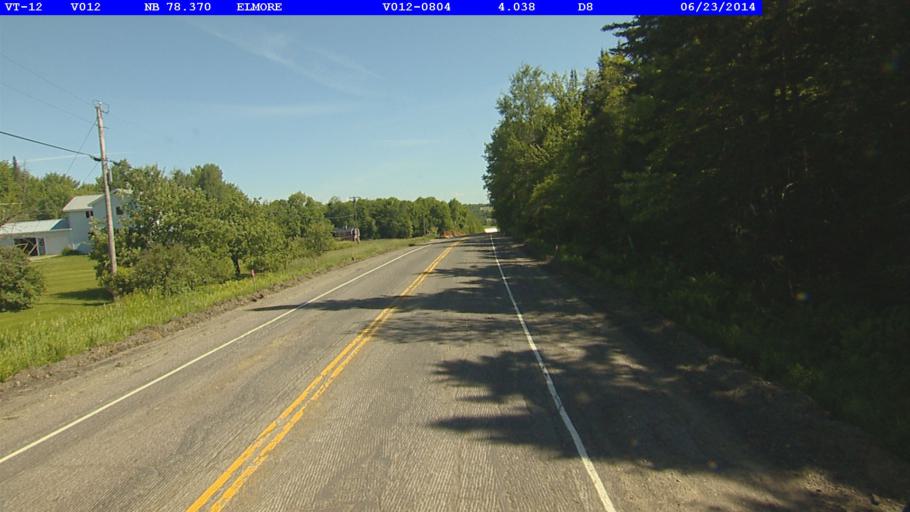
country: US
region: Vermont
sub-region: Lamoille County
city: Morrisville
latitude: 44.5035
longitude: -72.5165
